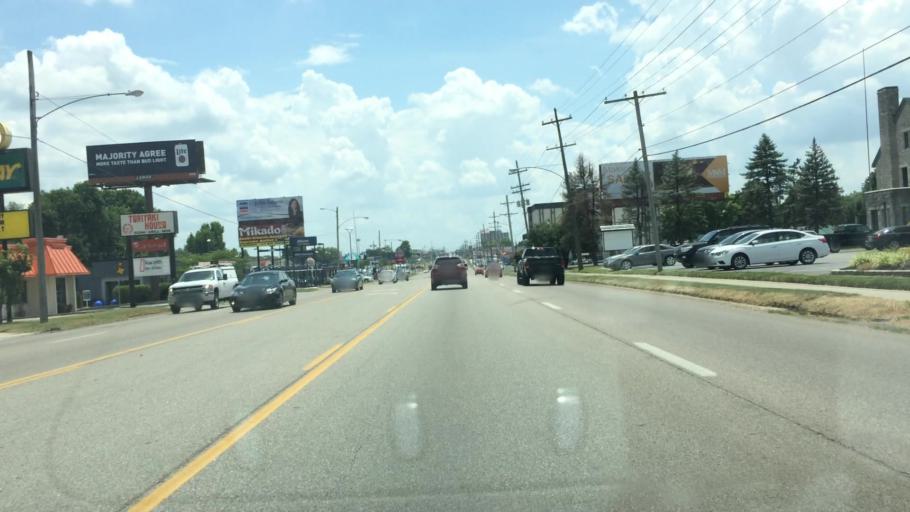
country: US
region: Missouri
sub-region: Greene County
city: Springfield
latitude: 37.1944
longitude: -93.2622
